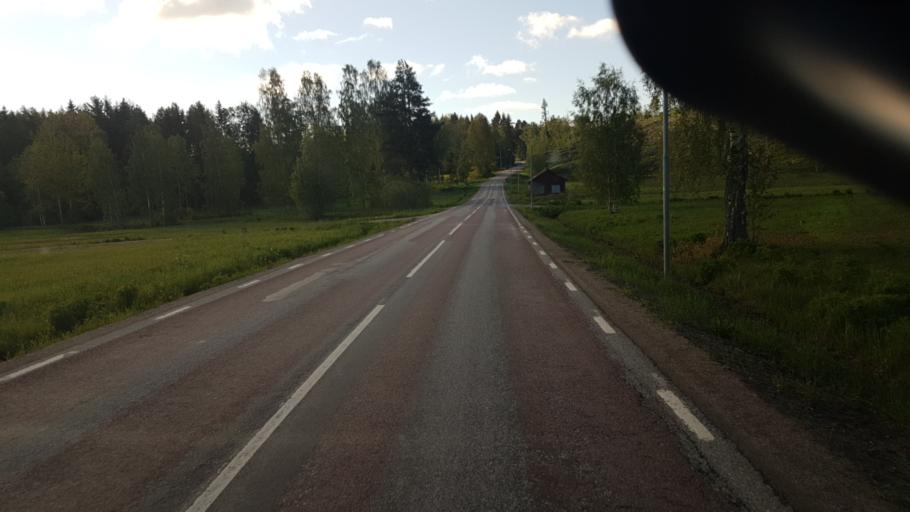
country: SE
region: Vaermland
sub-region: Arvika Kommun
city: Arvika
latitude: 59.5476
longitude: 12.5678
